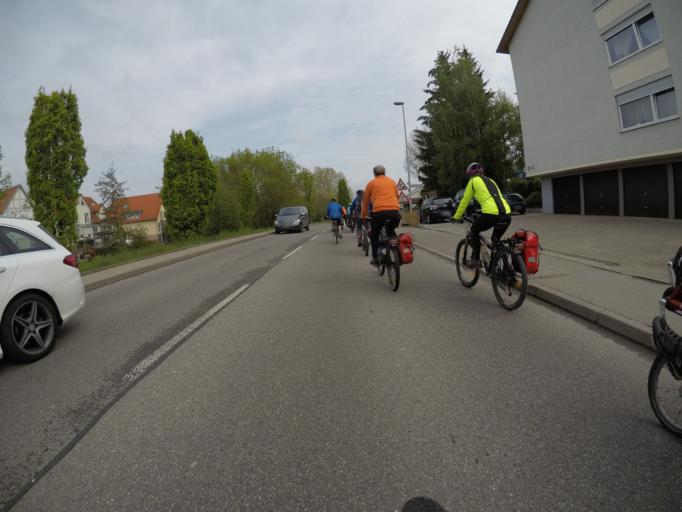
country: DE
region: Baden-Wuerttemberg
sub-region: Regierungsbezirk Stuttgart
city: Weil der Stadt
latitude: 48.7503
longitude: 8.8765
